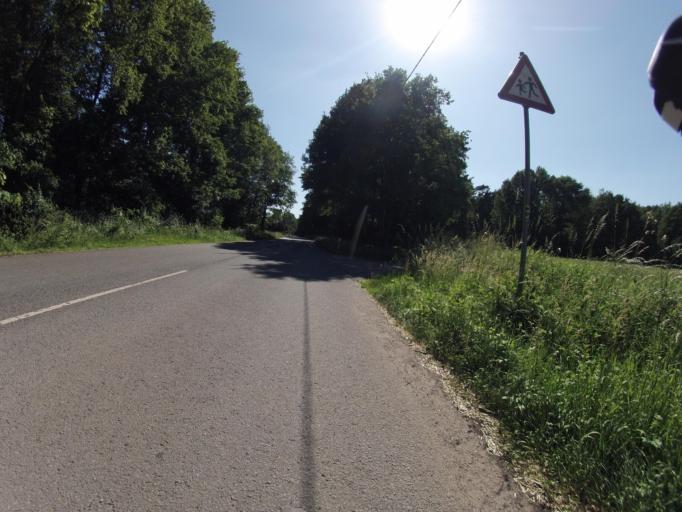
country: DE
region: North Rhine-Westphalia
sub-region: Regierungsbezirk Munster
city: Dreierwalde
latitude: 52.2640
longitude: 7.4760
